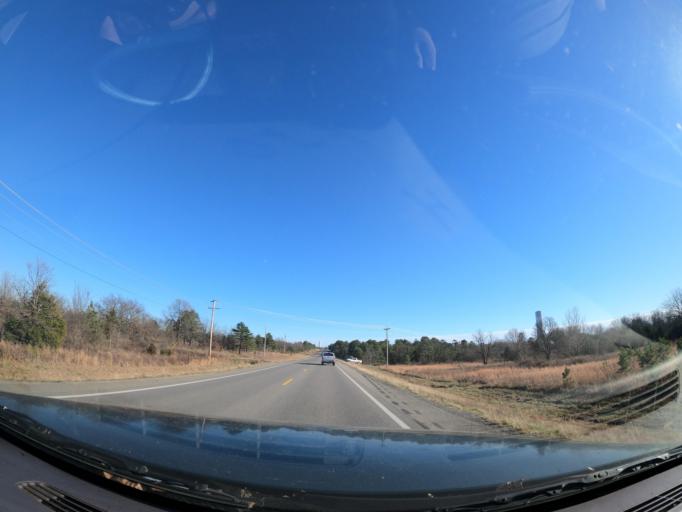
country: US
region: Oklahoma
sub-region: Pittsburg County
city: Longtown
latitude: 35.2336
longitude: -95.4605
